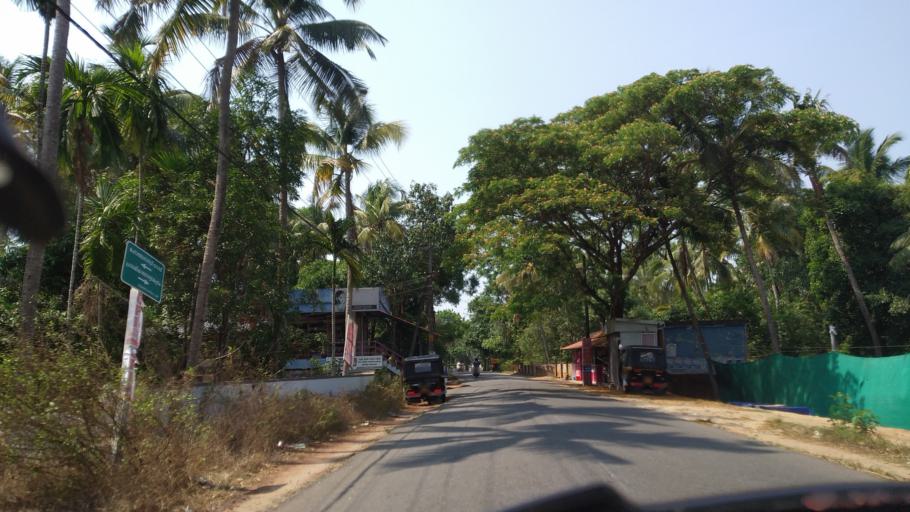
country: IN
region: Kerala
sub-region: Thrissur District
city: Kodungallur
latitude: 10.2378
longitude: 76.1528
